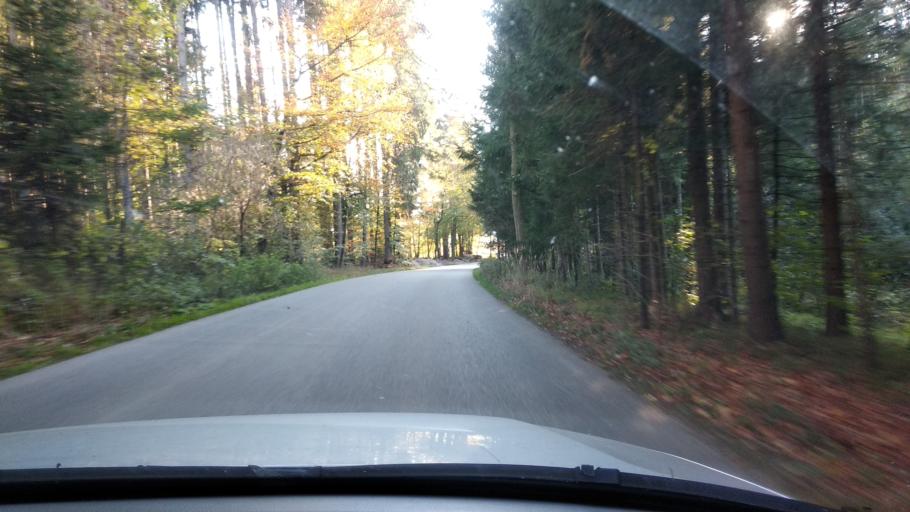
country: DE
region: Bavaria
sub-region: Upper Bavaria
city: Glonn
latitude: 47.9793
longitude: 11.8423
